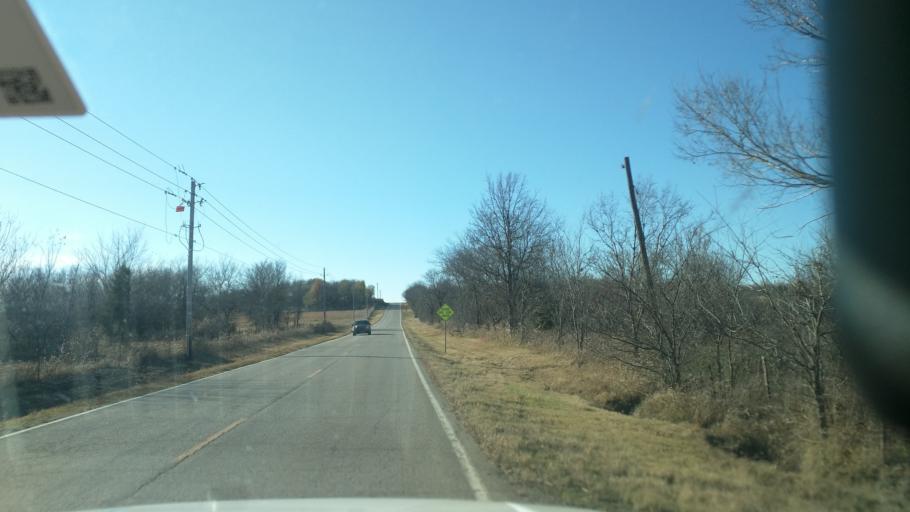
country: US
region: Oklahoma
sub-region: Nowata County
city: Nowata
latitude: 36.7717
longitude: -95.5695
